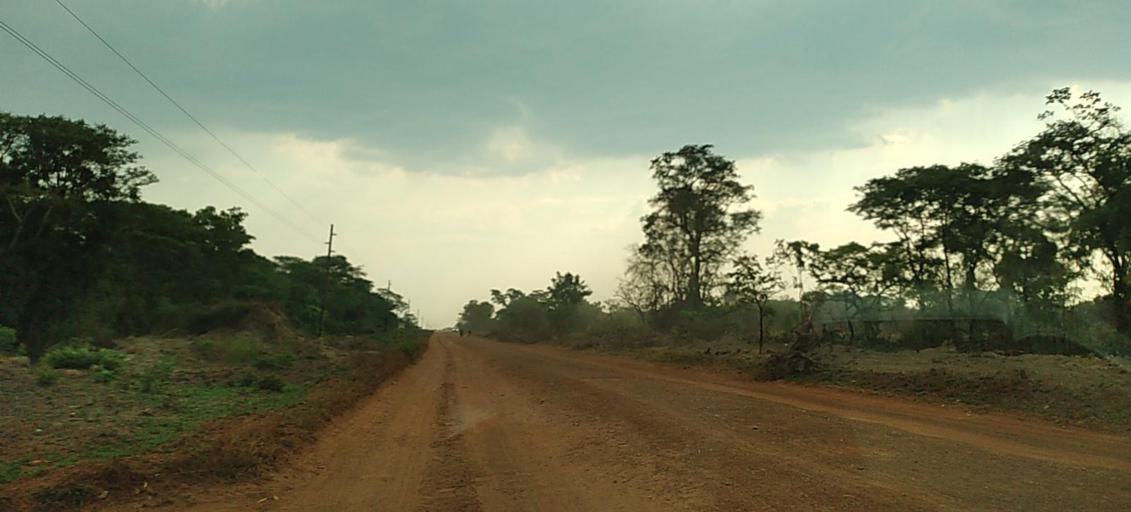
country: ZM
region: Copperbelt
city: Kalulushi
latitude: -12.9433
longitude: 27.9197
